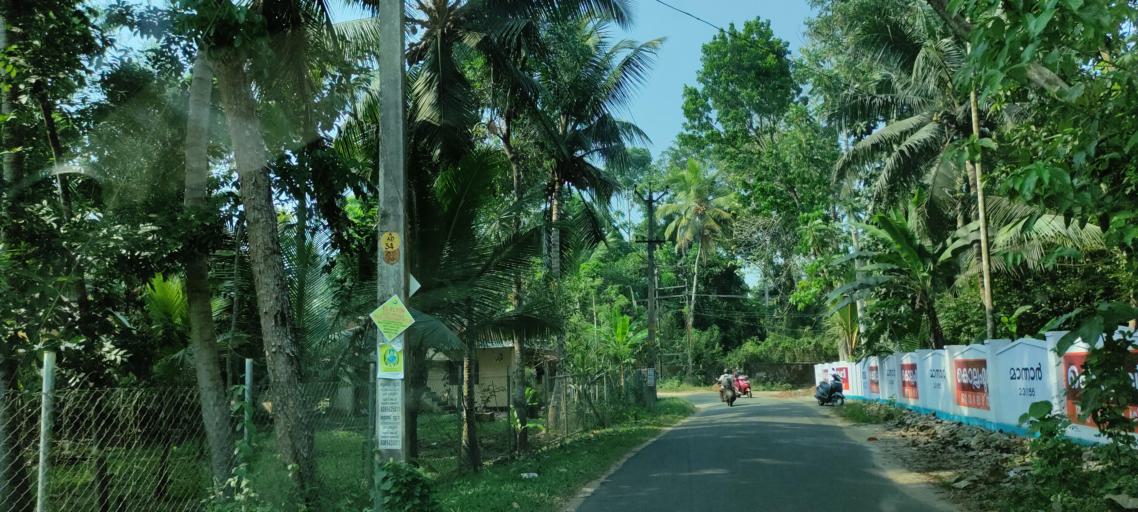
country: IN
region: Kerala
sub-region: Pattanamtitta
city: Tiruvalla
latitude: 9.3479
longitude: 76.5295
